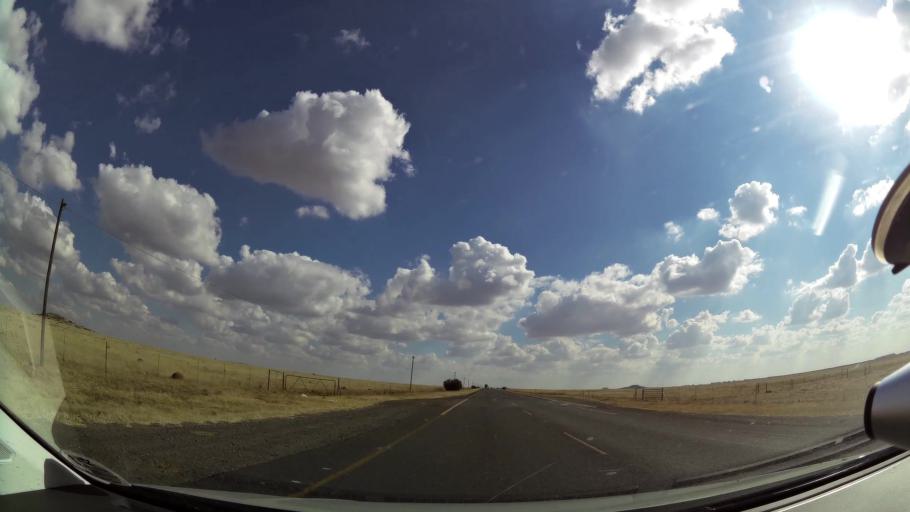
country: ZA
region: Orange Free State
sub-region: Mangaung Metropolitan Municipality
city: Bloemfontein
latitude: -29.1552
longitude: 25.7303
